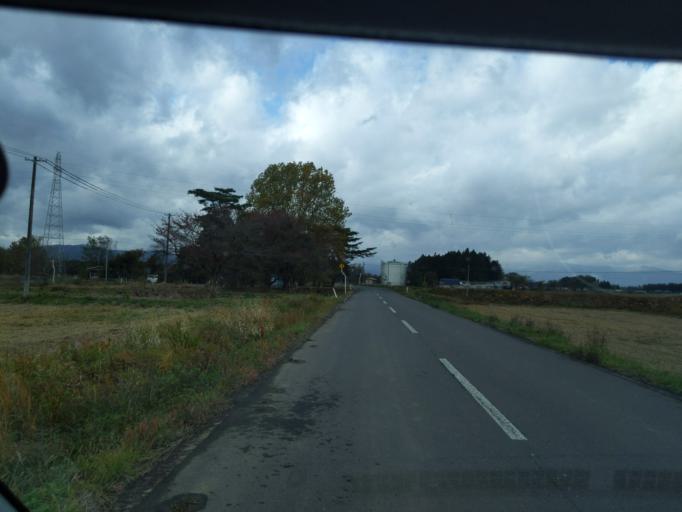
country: JP
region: Iwate
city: Mizusawa
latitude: 39.0645
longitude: 141.0853
